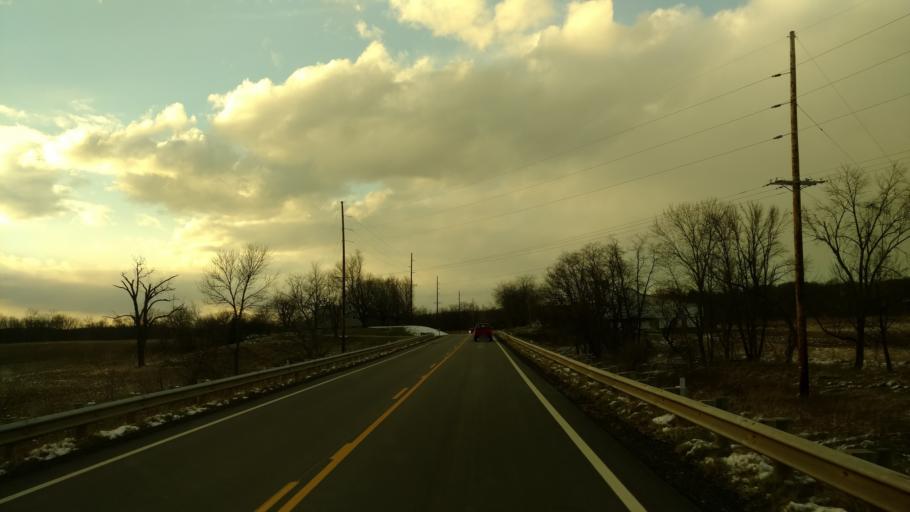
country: US
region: Ohio
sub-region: Ashland County
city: Ashland
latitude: 40.7947
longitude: -82.1900
